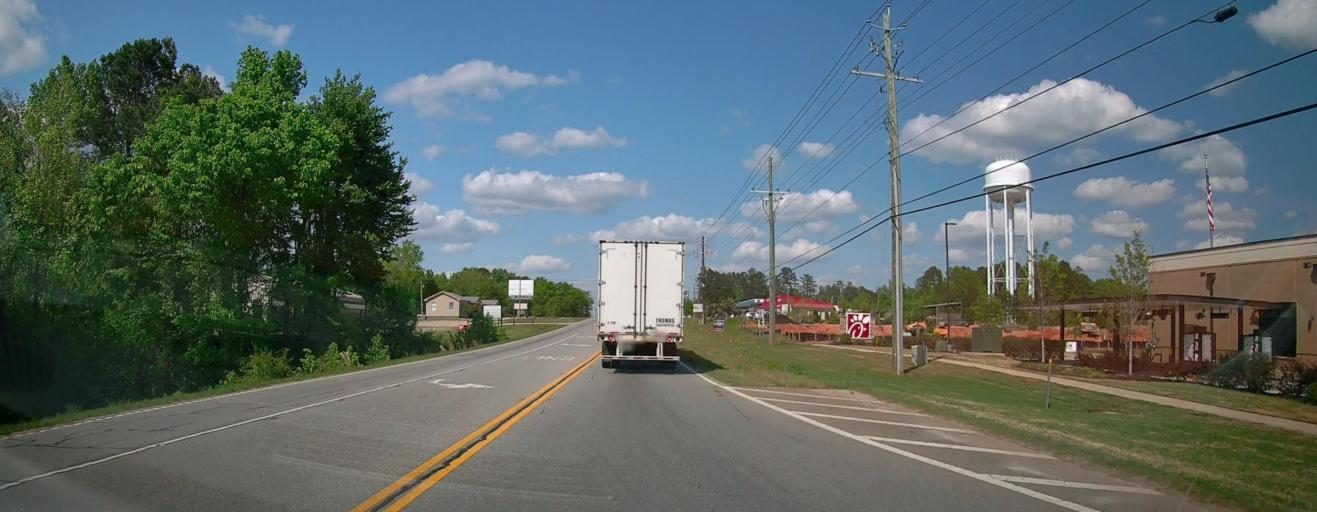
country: US
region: Georgia
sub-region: Greene County
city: Greensboro
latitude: 33.5417
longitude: -83.2087
